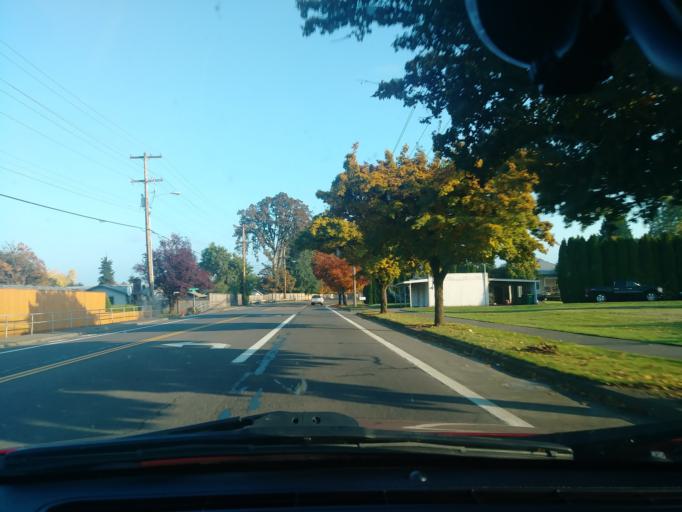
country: US
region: Oregon
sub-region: Washington County
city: Forest Grove
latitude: 45.5294
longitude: -123.1244
